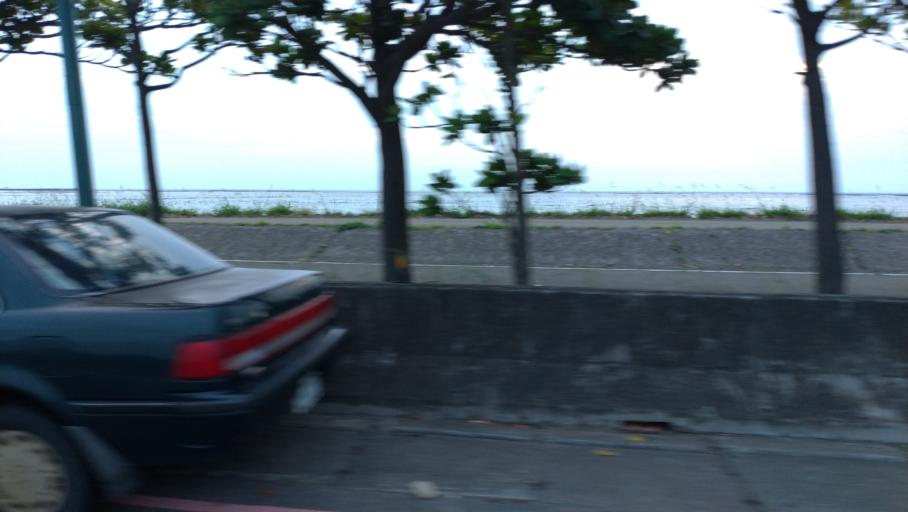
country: TW
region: Taiwan
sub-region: Hsinchu
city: Hsinchu
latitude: 24.7751
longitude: 120.9141
